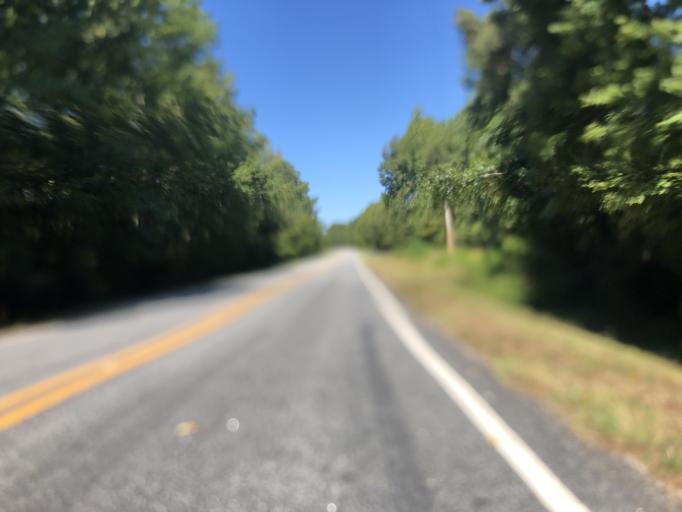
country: US
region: Georgia
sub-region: Heard County
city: Franklin
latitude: 33.3772
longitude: -84.9706
